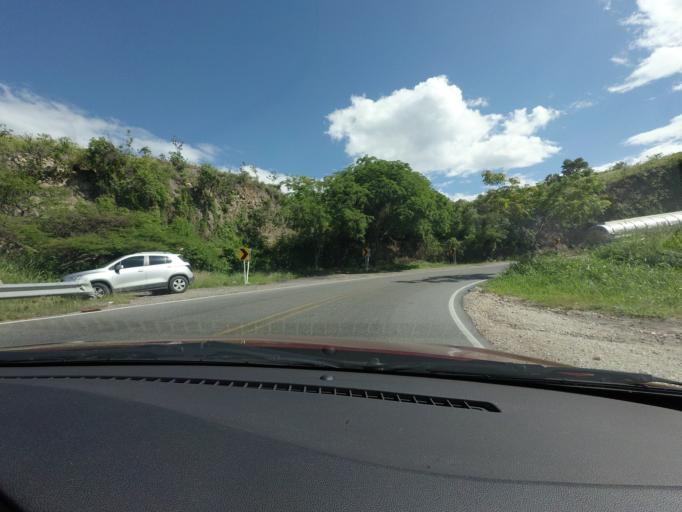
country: CO
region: Huila
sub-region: Gigante
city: Gigante
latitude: 2.4767
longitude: -75.5405
